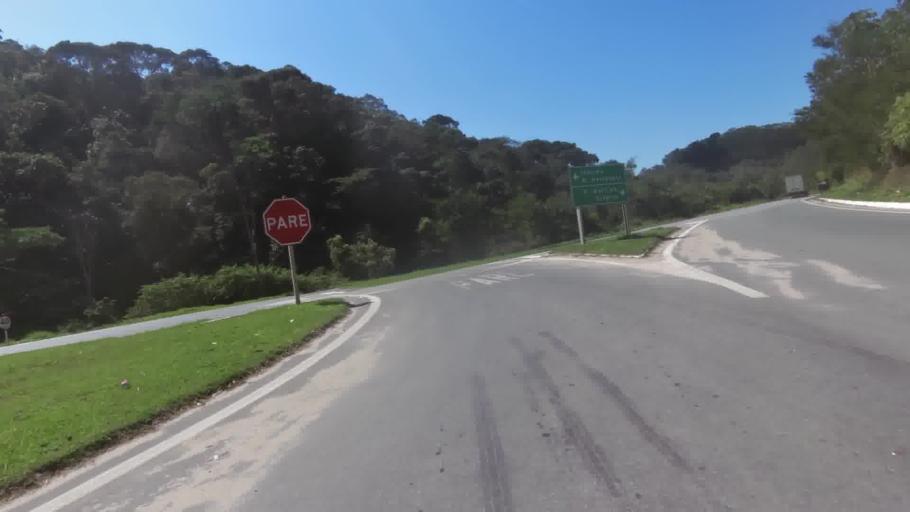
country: BR
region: Espirito Santo
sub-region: Marechal Floriano
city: Marechal Floriano
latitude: -20.4228
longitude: -40.7754
